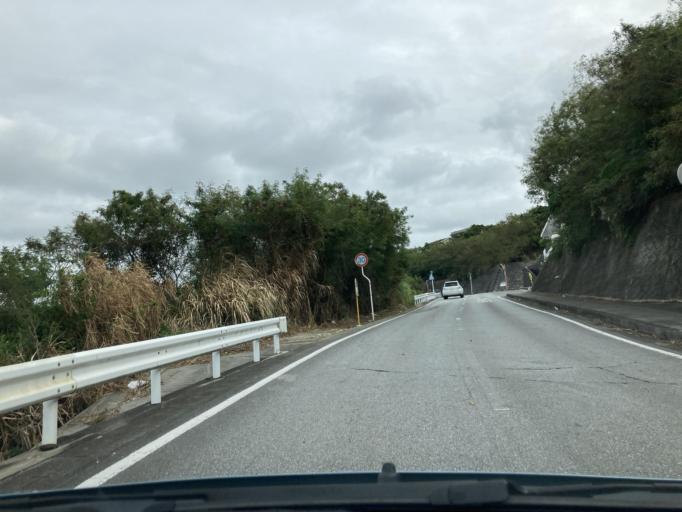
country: JP
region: Okinawa
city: Tomigusuku
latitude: 26.1610
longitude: 127.6747
